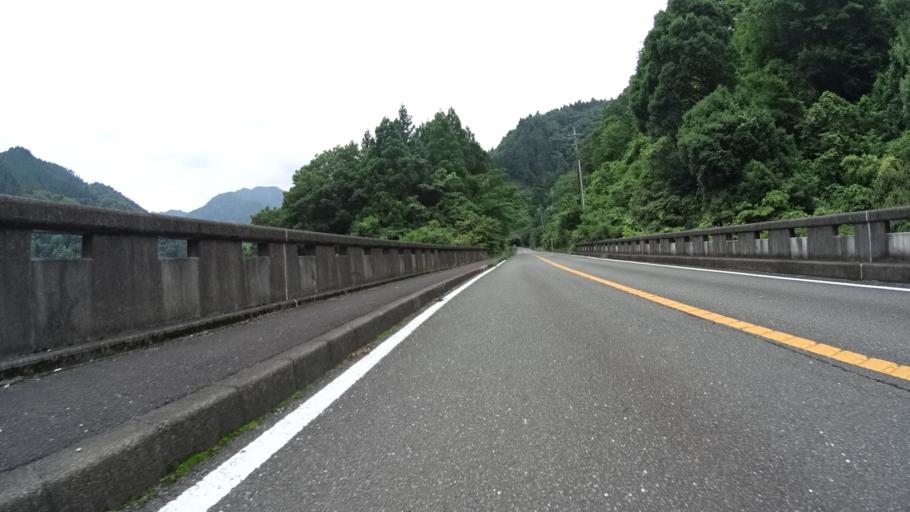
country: JP
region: Kanagawa
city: Hadano
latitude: 35.5151
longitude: 139.2329
